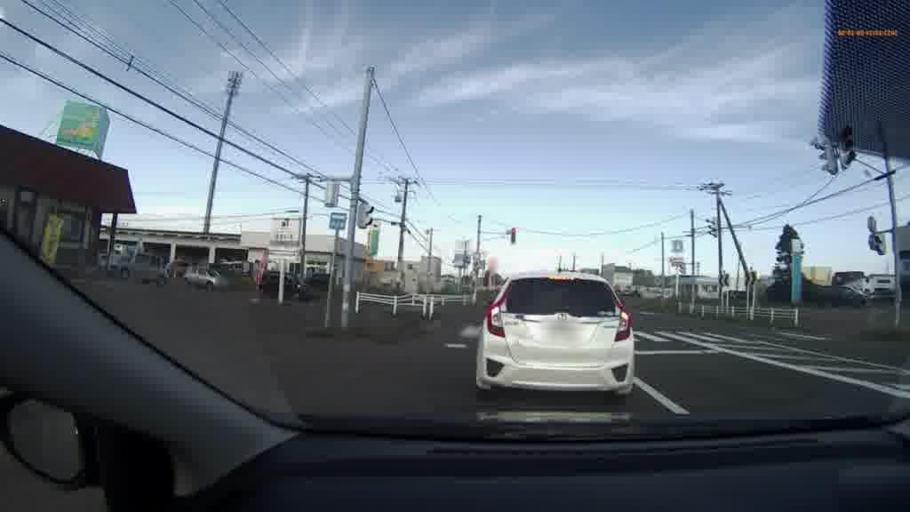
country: JP
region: Hokkaido
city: Kushiro
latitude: 43.0123
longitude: 144.4081
